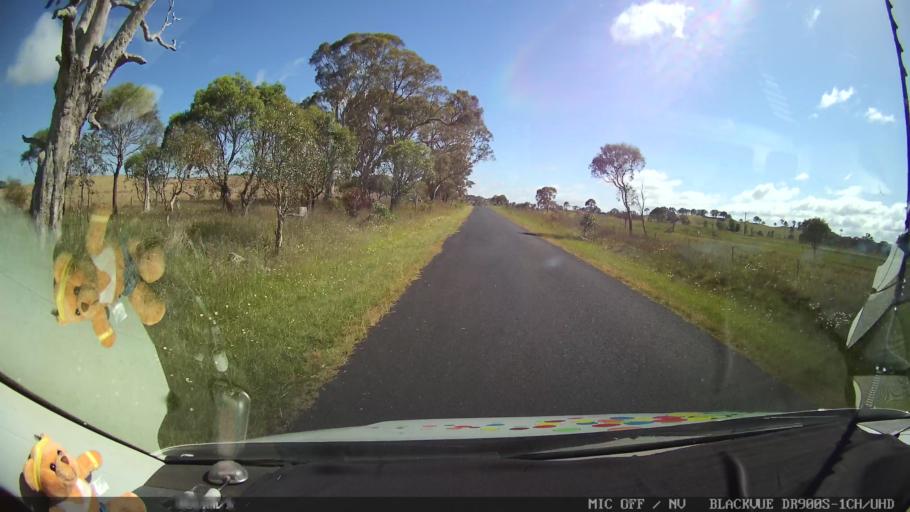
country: AU
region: New South Wales
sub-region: Guyra
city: Guyra
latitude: -30.1782
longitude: 151.6824
